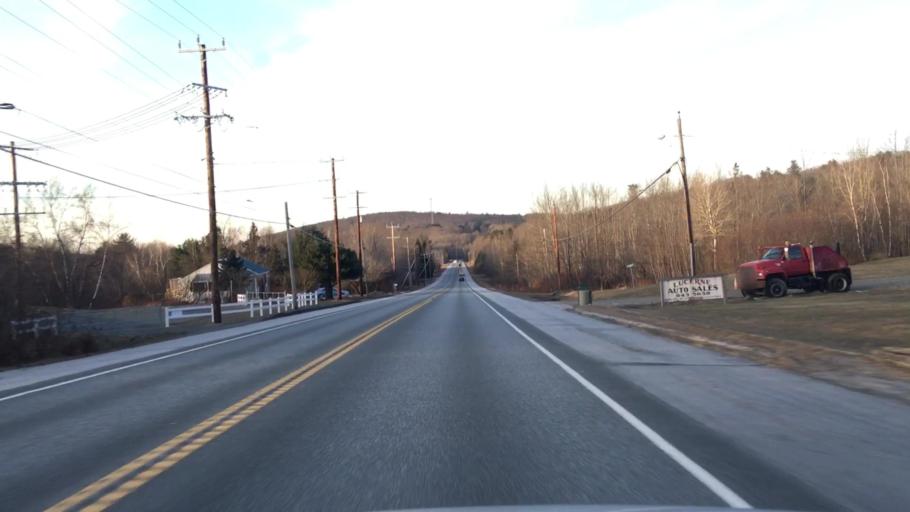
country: US
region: Maine
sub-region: Hancock County
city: Dedham
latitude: 44.7058
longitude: -68.6002
